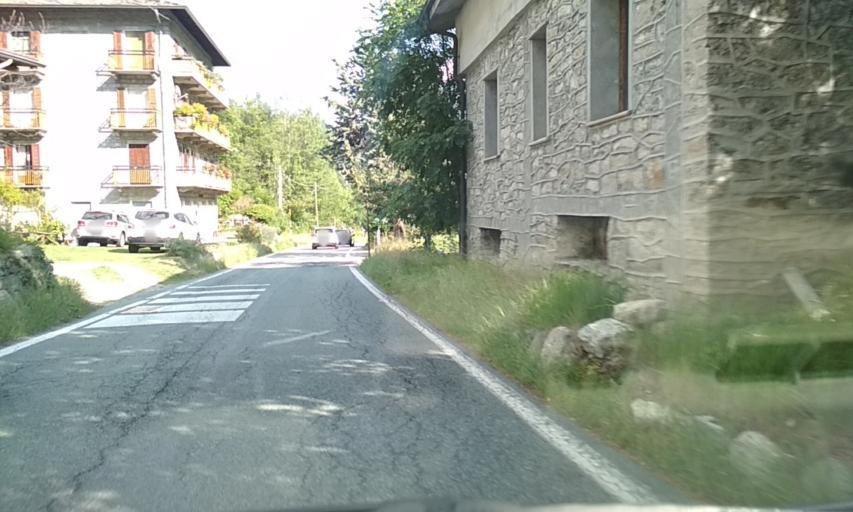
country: IT
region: Piedmont
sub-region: Provincia di Torino
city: Noasca
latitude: 45.4453
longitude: 7.3320
